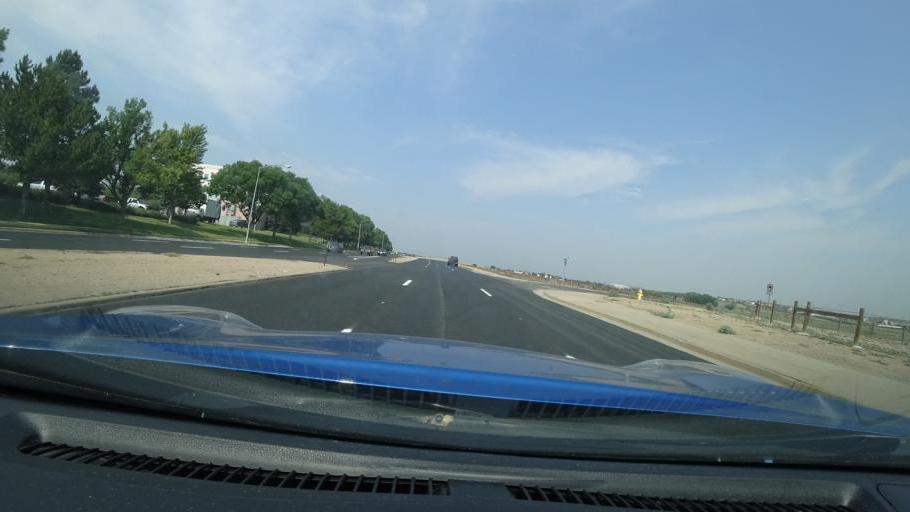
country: US
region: Colorado
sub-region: Adams County
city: Aurora
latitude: 39.7059
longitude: -104.7826
